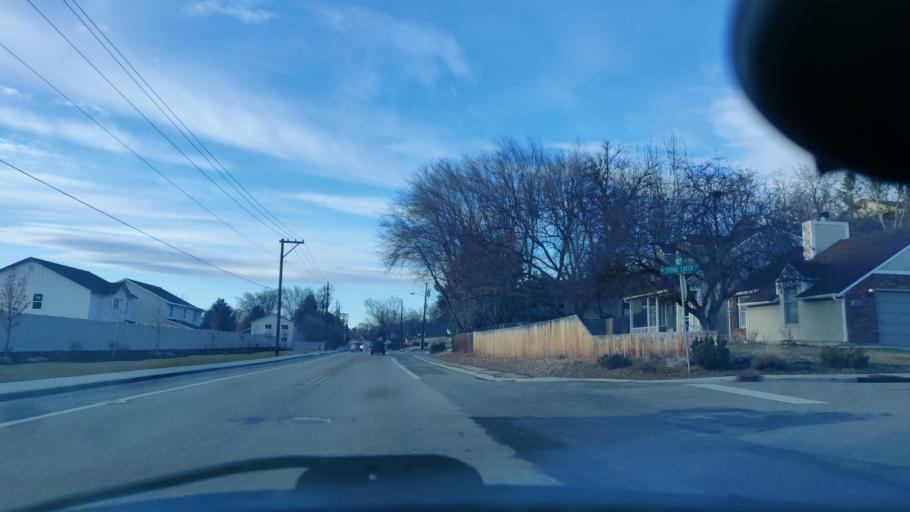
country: US
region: Idaho
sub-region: Ada County
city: Garden City
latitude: 43.6525
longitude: -116.2289
